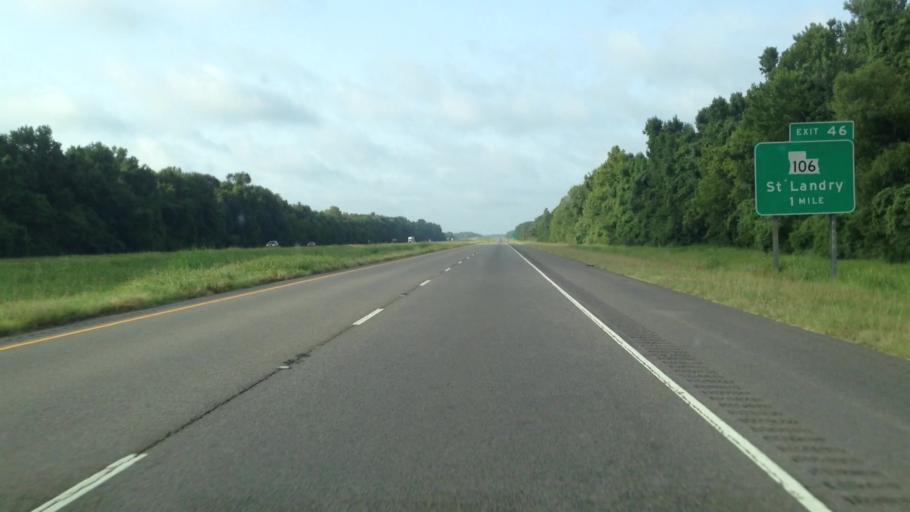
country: US
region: Louisiana
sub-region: Avoyelles Parish
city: Bunkie
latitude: 30.8866
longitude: -92.2274
